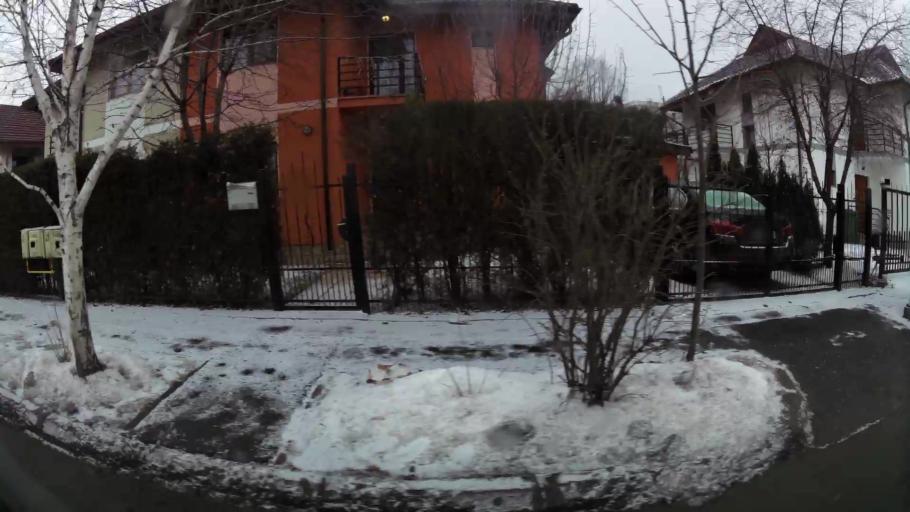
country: RO
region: Prahova
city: Ploiesti
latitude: 44.9569
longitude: 25.9954
